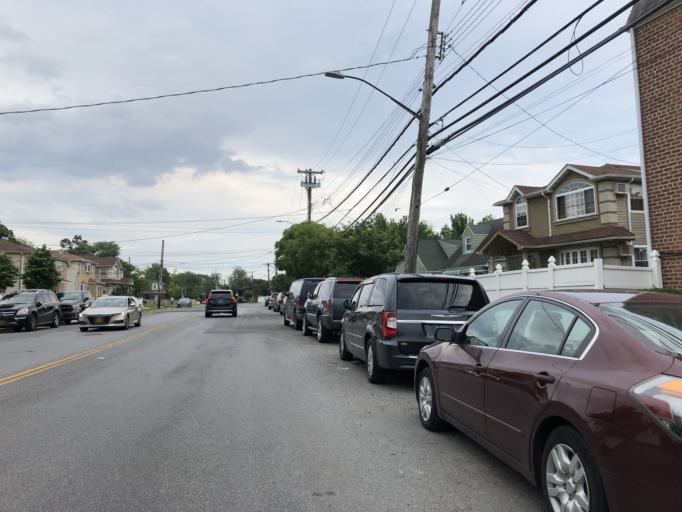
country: US
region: New York
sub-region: Nassau County
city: South Valley Stream
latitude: 40.6574
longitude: -73.7448
